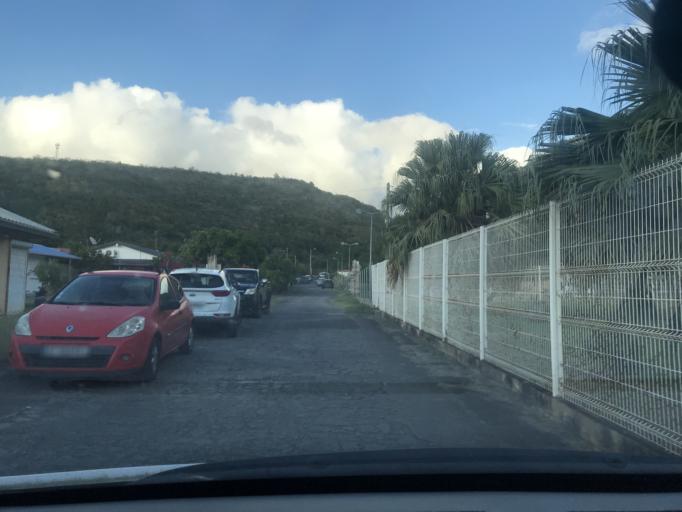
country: MQ
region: Martinique
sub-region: Martinique
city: Fort-de-France
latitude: 14.6345
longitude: -61.1304
